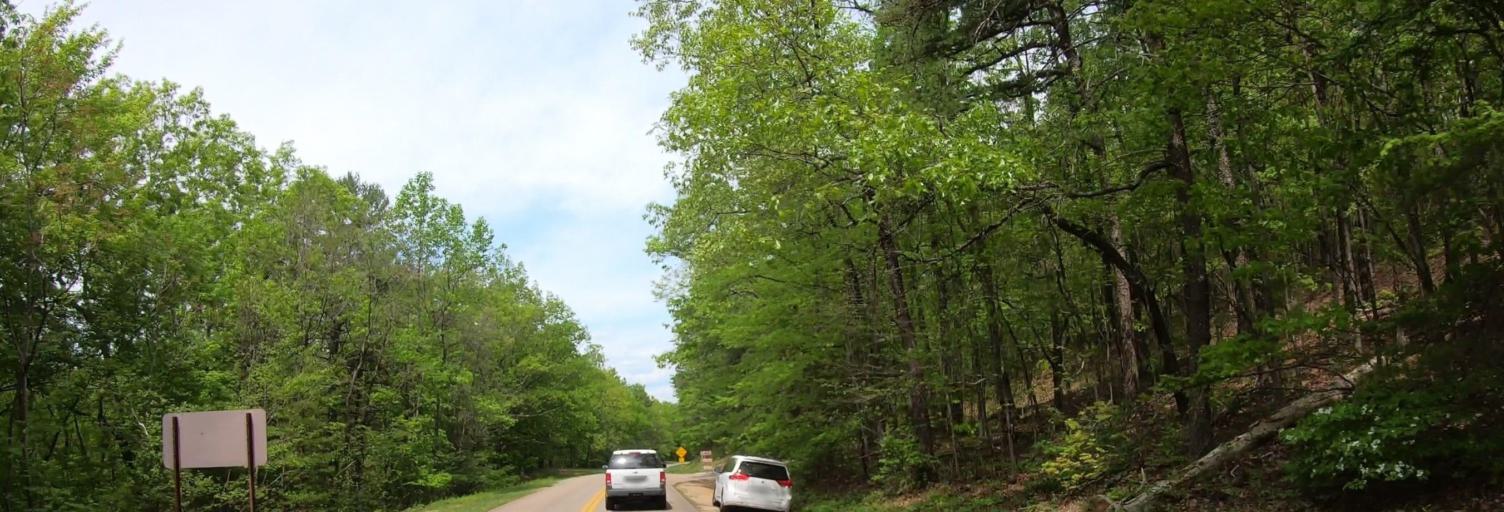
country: US
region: Virginia
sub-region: Roanoke County
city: Narrows
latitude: 37.2187
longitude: -79.9448
